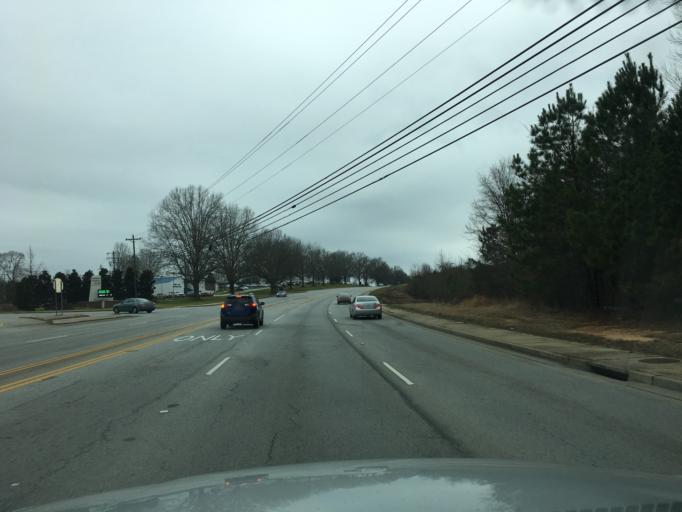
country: US
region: South Carolina
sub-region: Greenwood County
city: Greenwood
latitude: 34.2100
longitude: -82.1165
